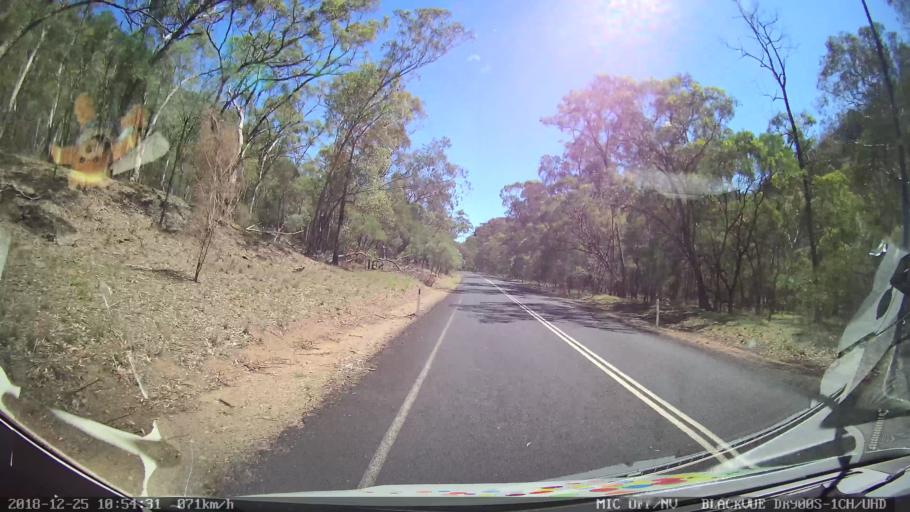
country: AU
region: New South Wales
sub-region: Upper Hunter Shire
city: Merriwa
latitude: -32.4089
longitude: 150.2734
